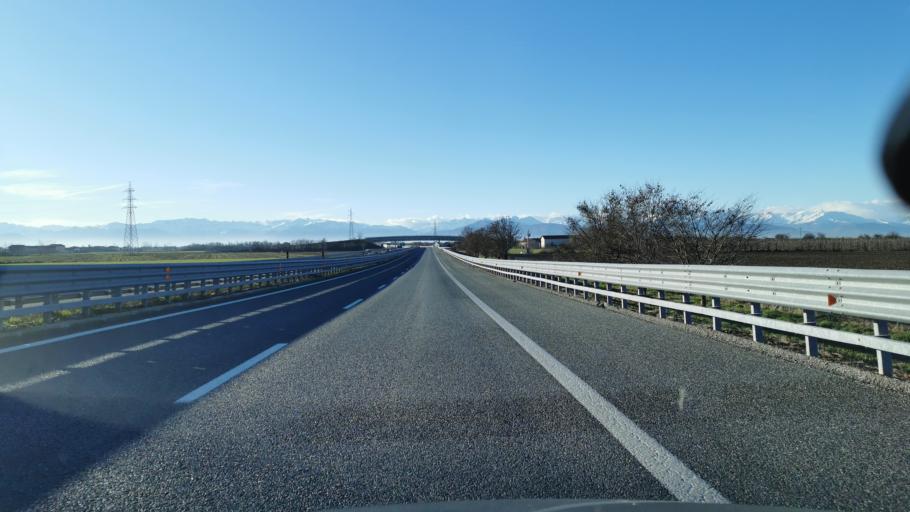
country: IT
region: Piedmont
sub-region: Provincia di Cuneo
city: Trinita
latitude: 44.4699
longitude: 7.7457
